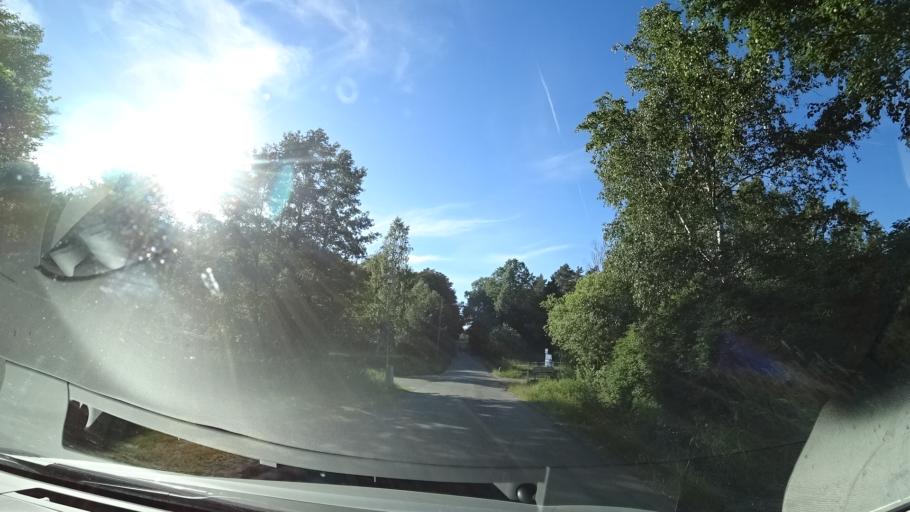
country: SE
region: Vaestra Goetaland
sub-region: Goteborg
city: Billdal
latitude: 57.5852
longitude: 11.9744
